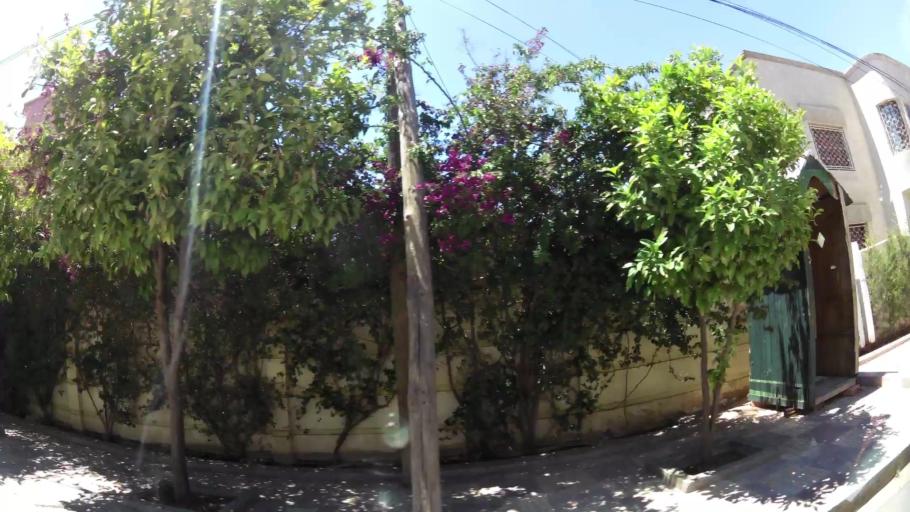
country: MA
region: Meknes-Tafilalet
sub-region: Meknes
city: Meknes
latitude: 33.9105
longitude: -5.5628
